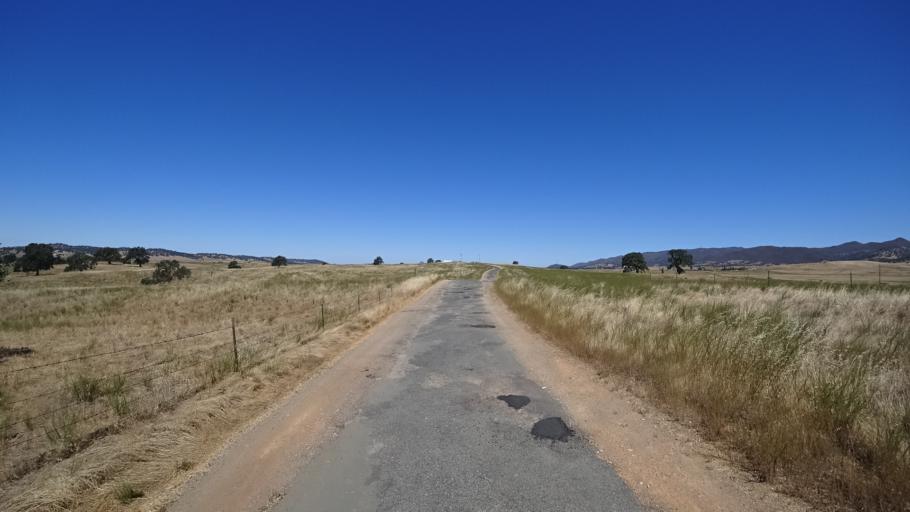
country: US
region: California
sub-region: Calaveras County
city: Copperopolis
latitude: 38.0367
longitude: -120.7259
